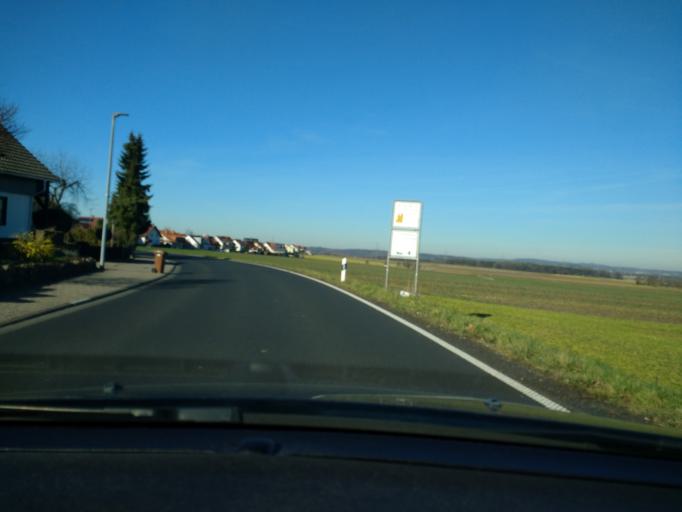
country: DE
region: Bavaria
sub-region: Regierungsbezirk Unterfranken
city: Geiselbach
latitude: 50.1421
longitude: 9.1252
